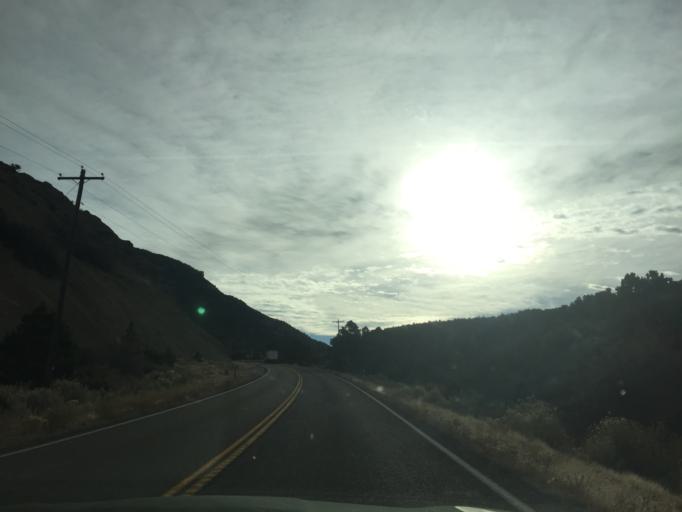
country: US
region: Utah
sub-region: Iron County
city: Cedar City
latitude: 37.6668
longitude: -113.0091
